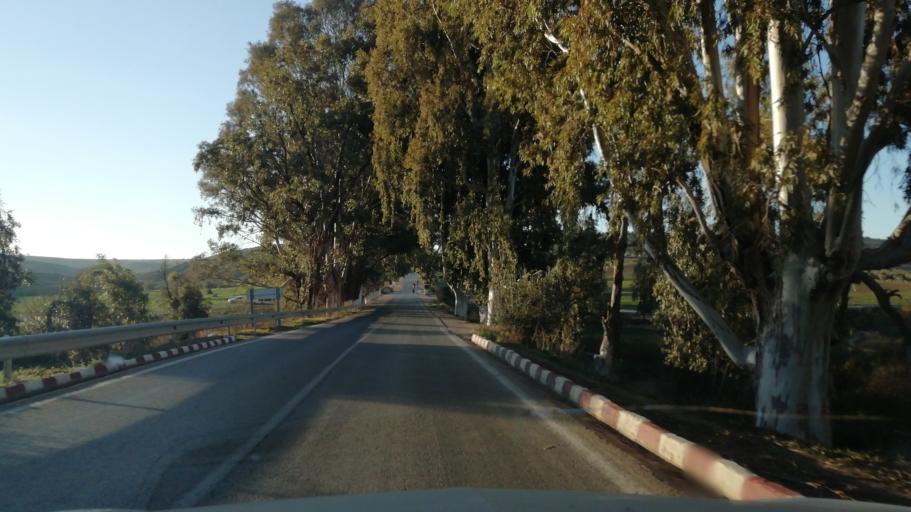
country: DZ
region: Tlemcen
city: Nedroma
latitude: 34.8263
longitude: -1.6545
